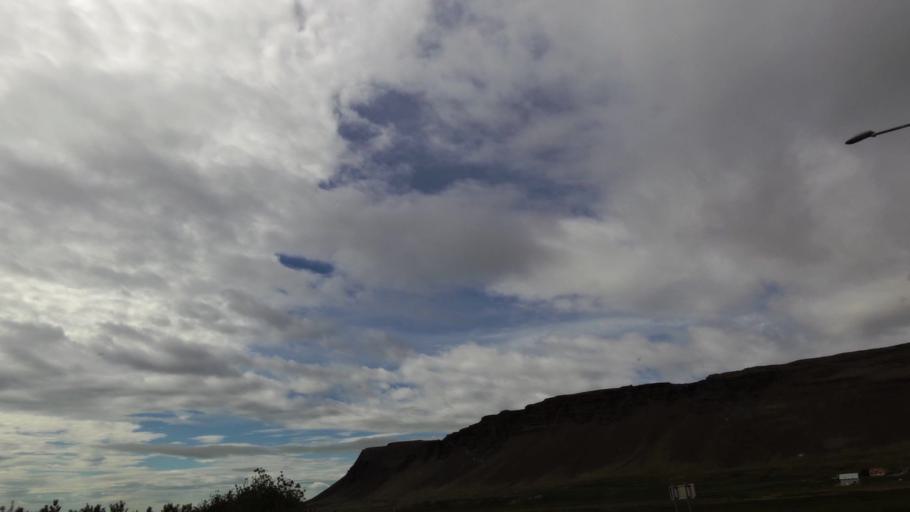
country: IS
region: West
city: Stykkisholmur
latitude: 65.4513
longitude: -22.2022
